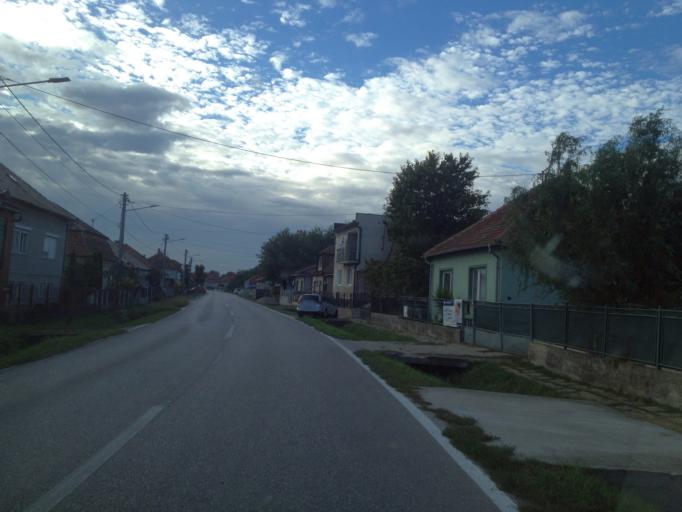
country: HU
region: Komarom-Esztergom
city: Almasfuzito
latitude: 47.7530
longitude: 18.2195
